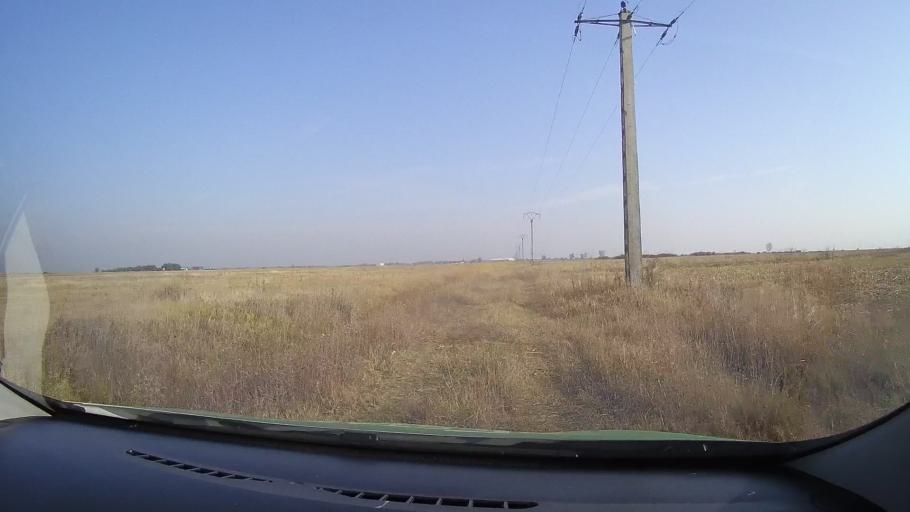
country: RO
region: Arad
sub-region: Comuna Pilu
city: Pilu
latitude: 46.5562
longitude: 21.3365
